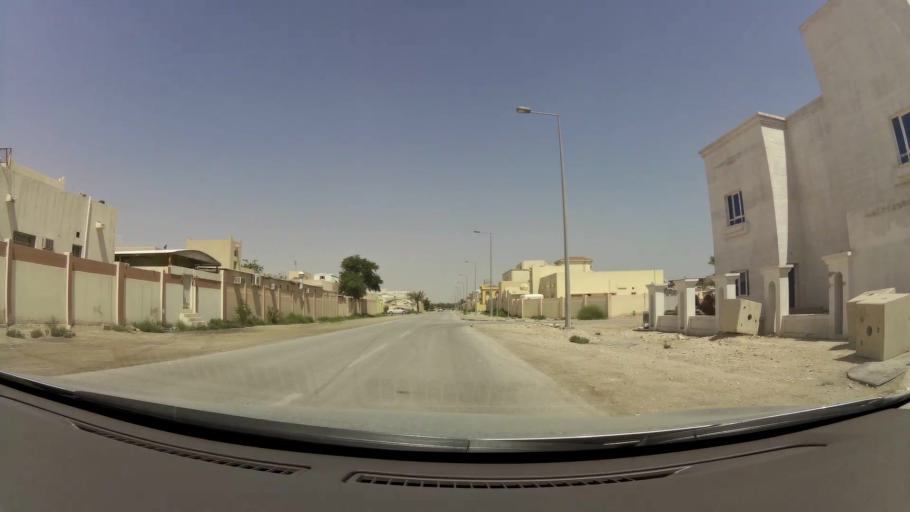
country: QA
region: Baladiyat Umm Salal
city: Umm Salal Muhammad
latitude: 25.3757
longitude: 51.4756
